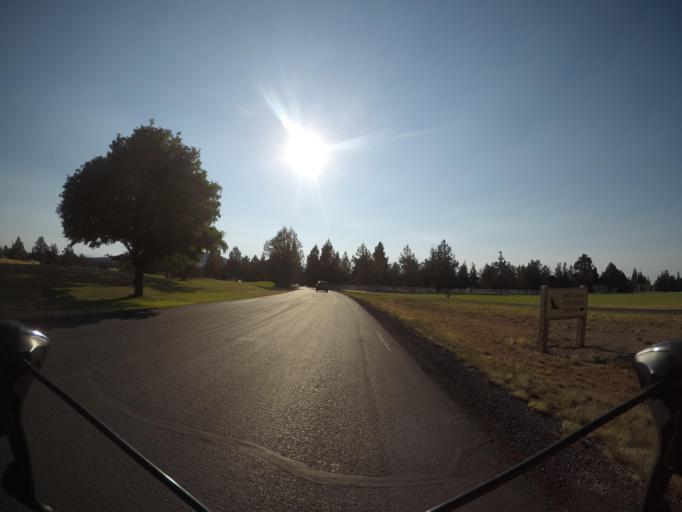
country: US
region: Oregon
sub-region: Deschutes County
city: Redmond
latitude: 44.2634
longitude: -121.2556
